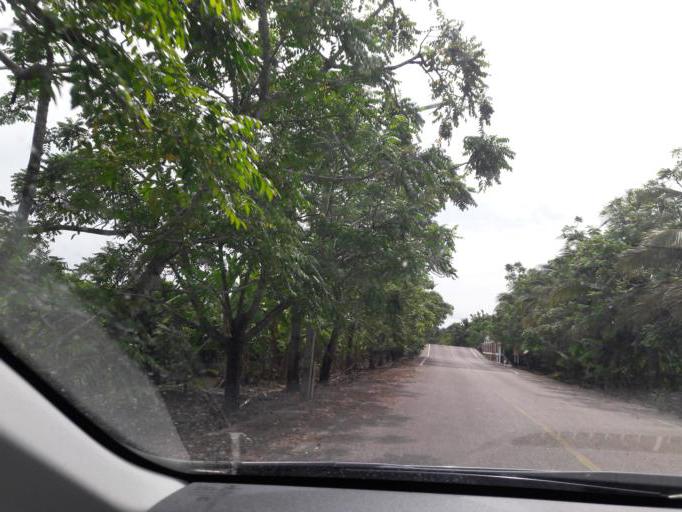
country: TH
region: Ratchaburi
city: Damnoen Saduak
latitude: 13.5209
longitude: 99.9967
